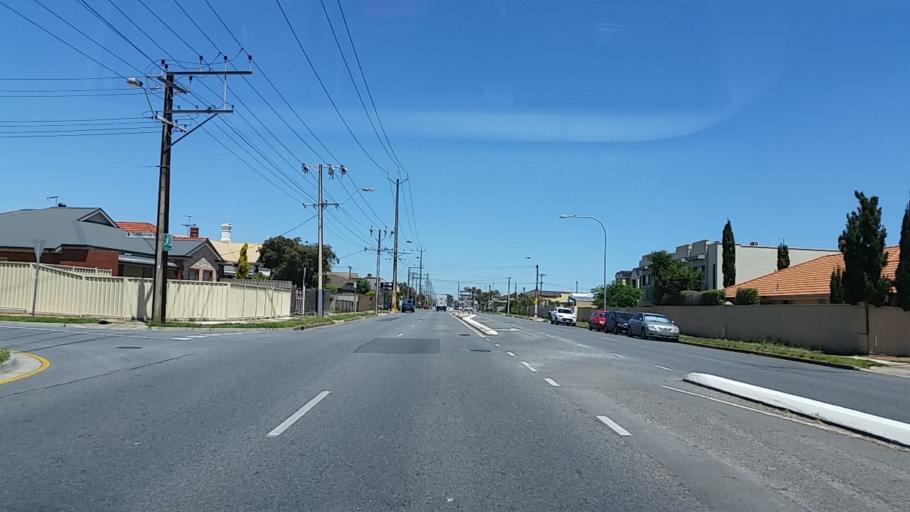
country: AU
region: South Australia
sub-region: Charles Sturt
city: Woodville West
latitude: -34.8871
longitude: 138.5313
